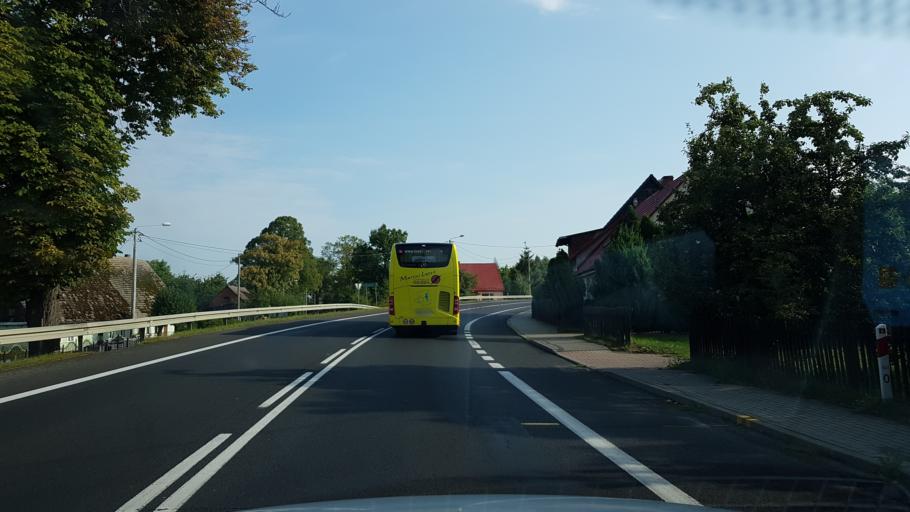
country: PL
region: West Pomeranian Voivodeship
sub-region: Powiat koszalinski
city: Sianow
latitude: 54.2726
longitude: 16.4271
